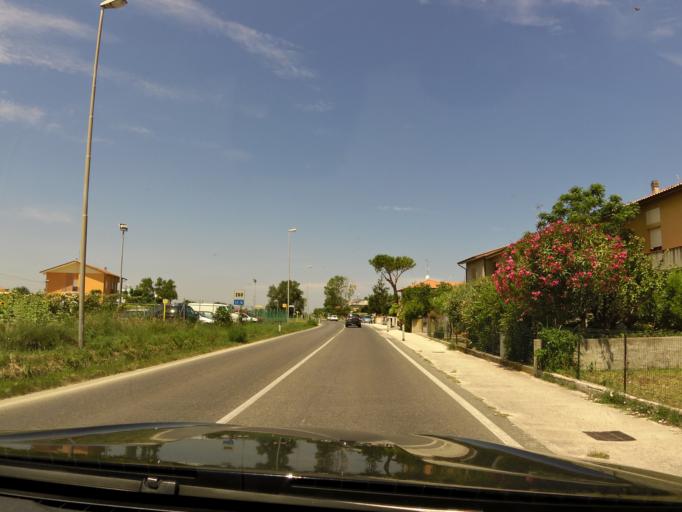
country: IT
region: The Marches
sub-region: Provincia di Pesaro e Urbino
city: Marotta
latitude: 43.7897
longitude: 13.1062
